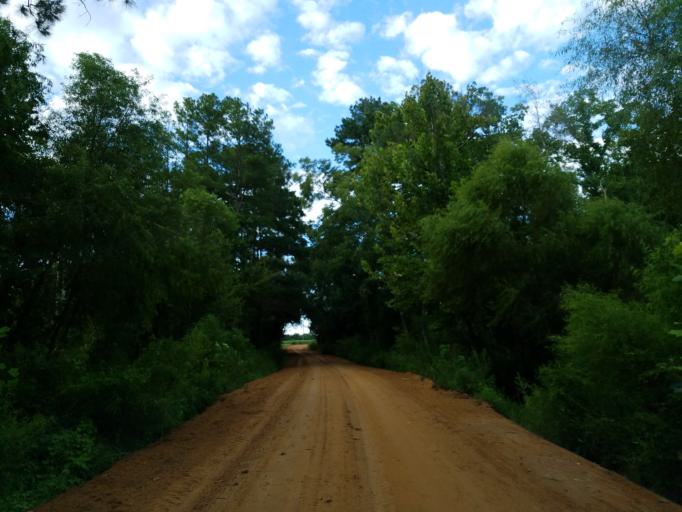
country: US
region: Georgia
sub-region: Cook County
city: Sparks
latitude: 31.2291
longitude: -83.4774
